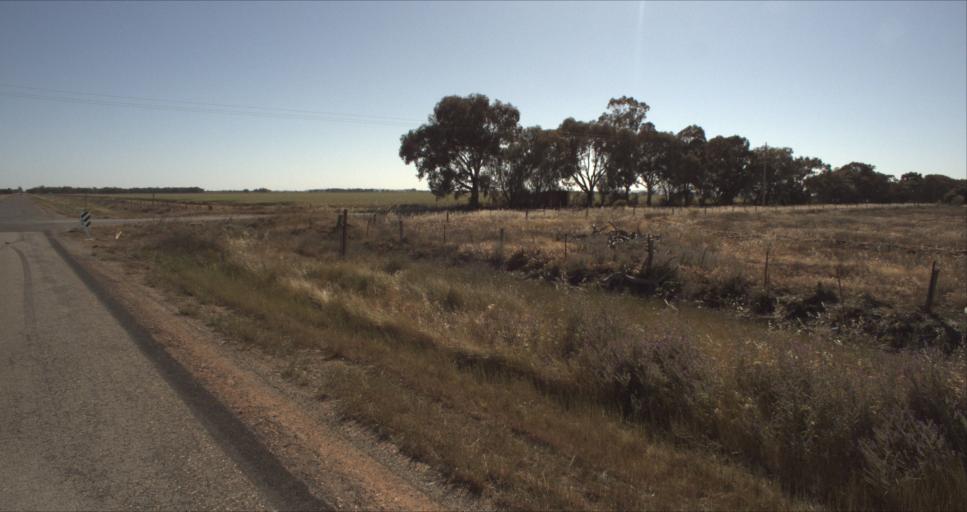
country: AU
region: New South Wales
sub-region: Leeton
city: Leeton
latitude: -34.5780
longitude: 146.2622
